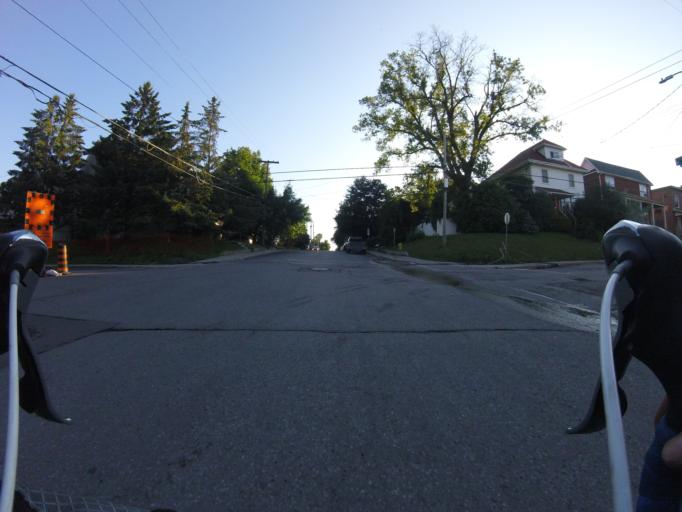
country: CA
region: Ontario
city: Ottawa
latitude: 45.3995
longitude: -75.7133
